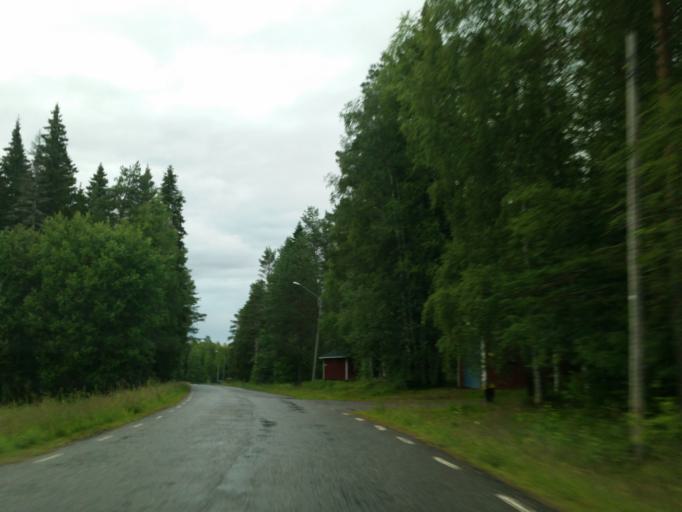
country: SE
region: Vaesterbotten
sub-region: Robertsfors Kommun
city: Robertsfors
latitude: 64.0351
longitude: 20.8503
